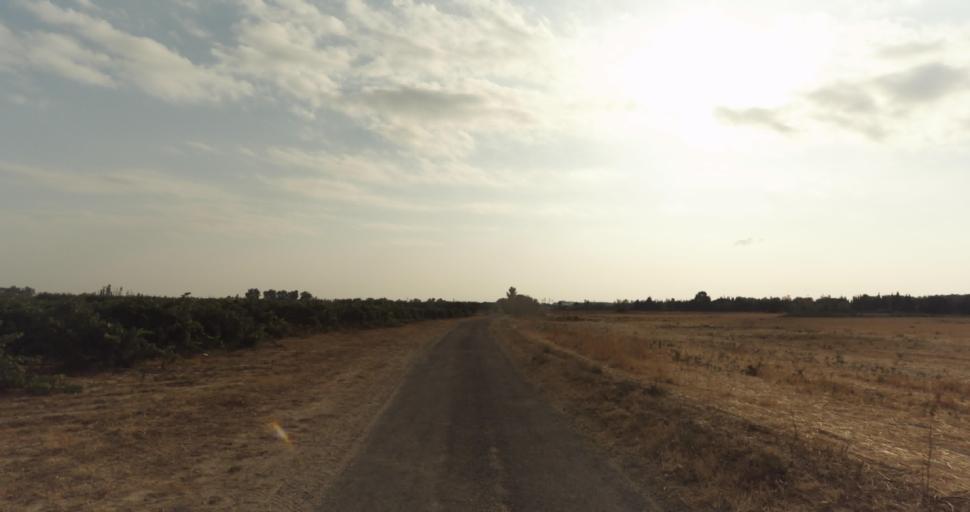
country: FR
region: Languedoc-Roussillon
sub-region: Departement des Pyrenees-Orientales
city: Theza
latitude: 42.6312
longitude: 2.9344
